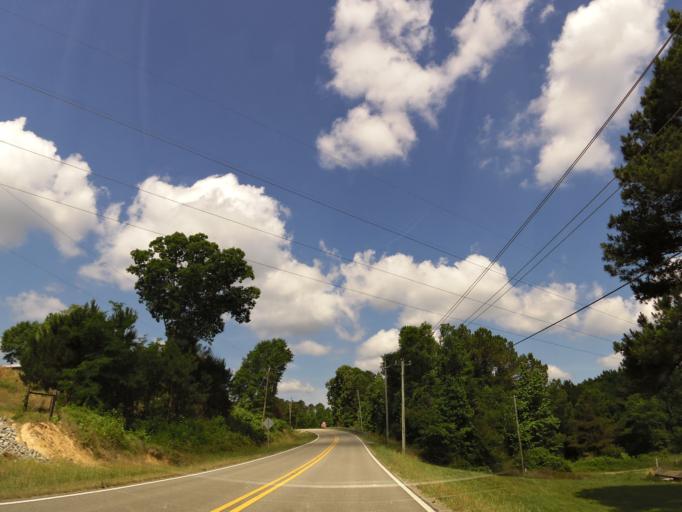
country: US
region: Alabama
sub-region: Marion County
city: Guin
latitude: 33.9835
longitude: -87.8892
